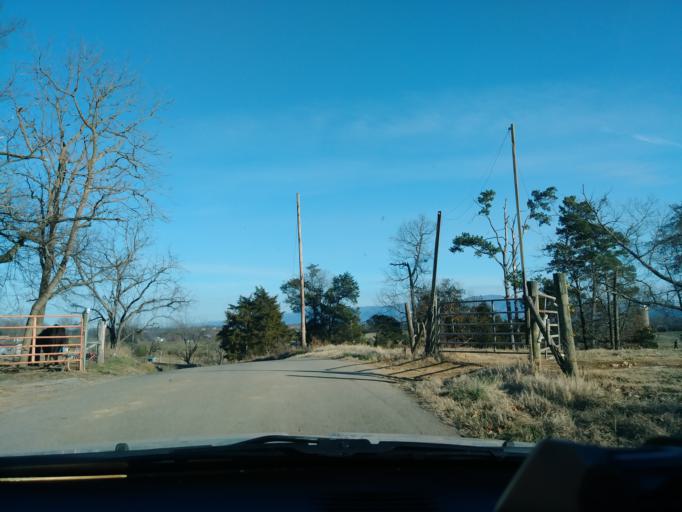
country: US
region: Tennessee
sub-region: Greene County
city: Greeneville
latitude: 36.0865
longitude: -82.9039
